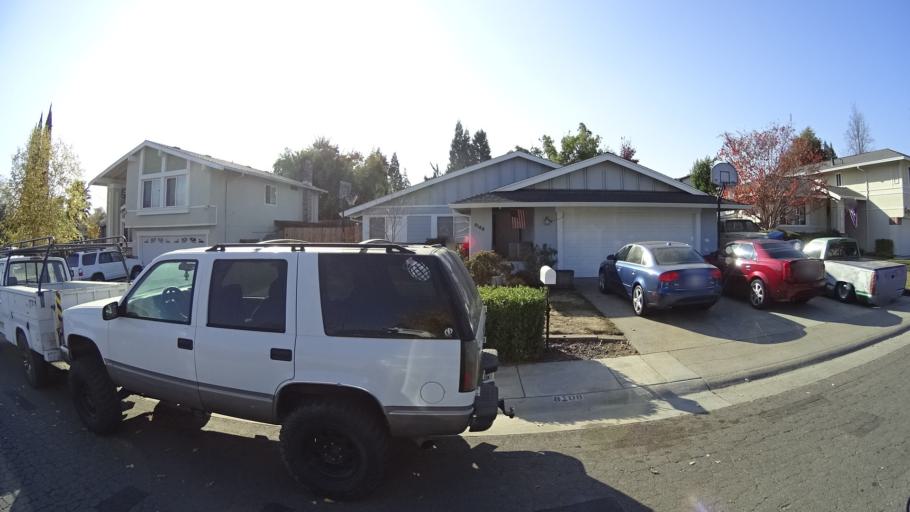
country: US
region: California
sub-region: Sacramento County
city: Citrus Heights
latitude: 38.7136
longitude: -121.2614
